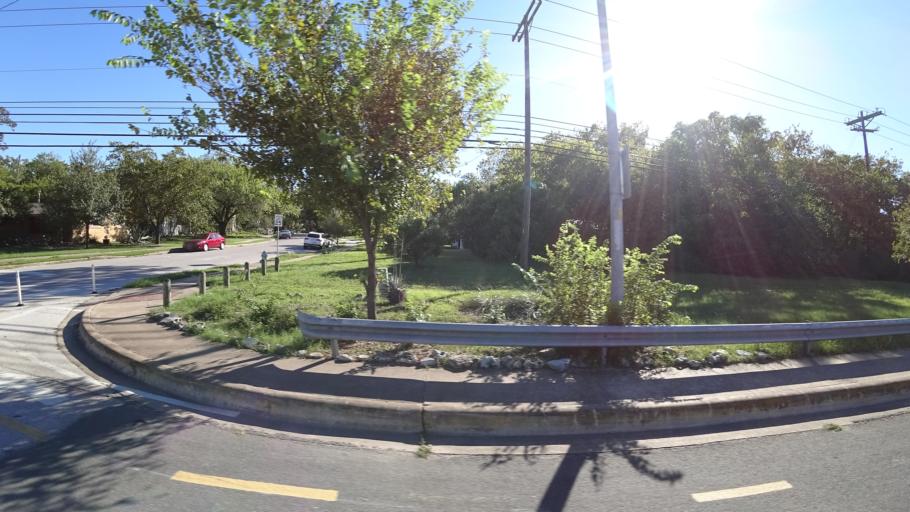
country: US
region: Texas
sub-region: Travis County
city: West Lake Hills
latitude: 30.3300
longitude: -97.7542
